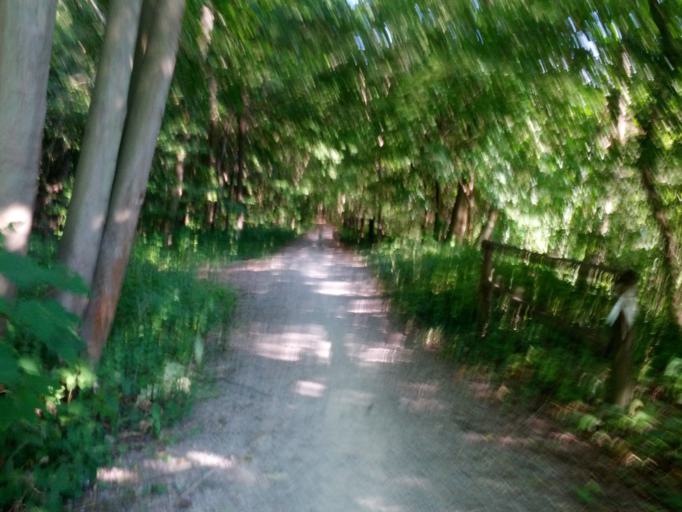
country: DE
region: Thuringia
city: Creuzburg
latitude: 51.0631
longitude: 10.2745
